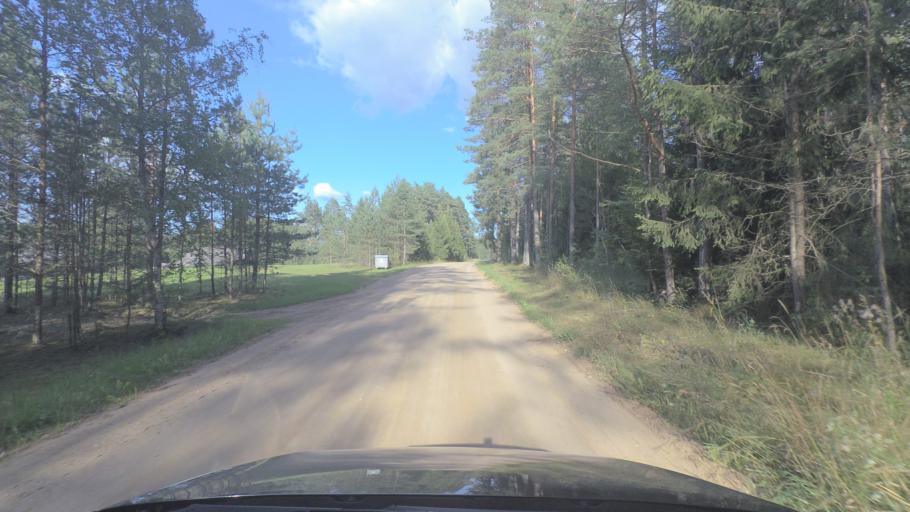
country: LT
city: Pabrade
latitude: 55.1478
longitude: 25.7593
